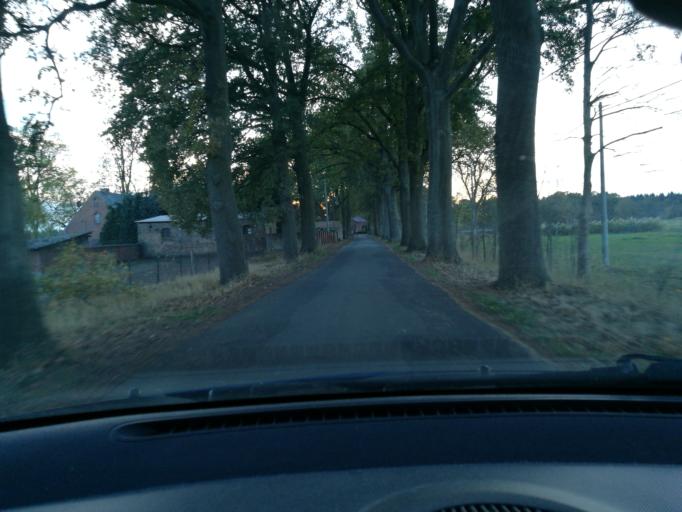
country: DE
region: Brandenburg
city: Cumlosen
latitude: 53.0813
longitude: 11.6544
